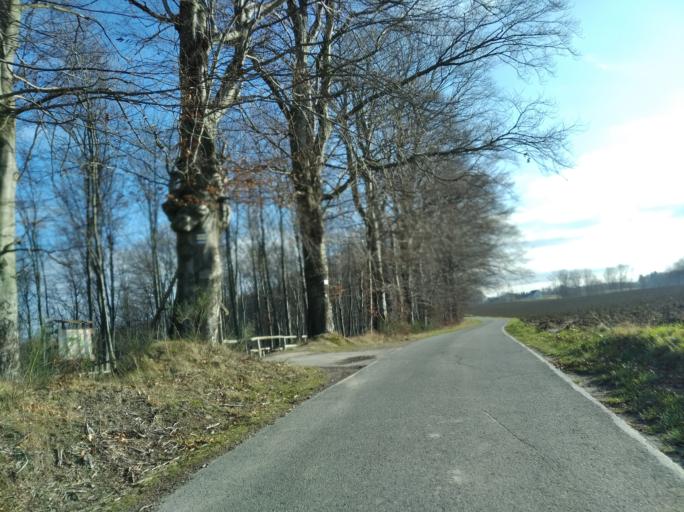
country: PL
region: Subcarpathian Voivodeship
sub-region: Powiat strzyzowski
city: Czudec
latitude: 49.9199
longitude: 21.8375
